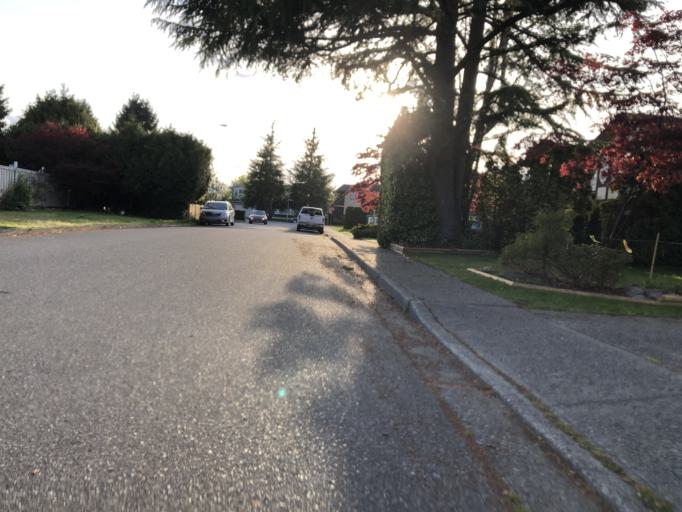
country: CA
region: British Columbia
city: Richmond
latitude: 49.1440
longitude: -123.1079
